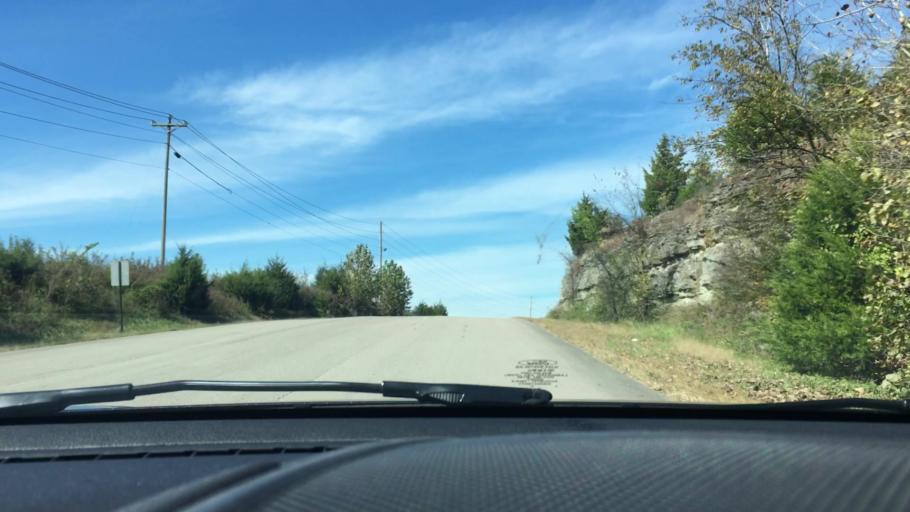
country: US
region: Tennessee
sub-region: Giles County
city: Pulaski
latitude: 35.2231
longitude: -87.0668
